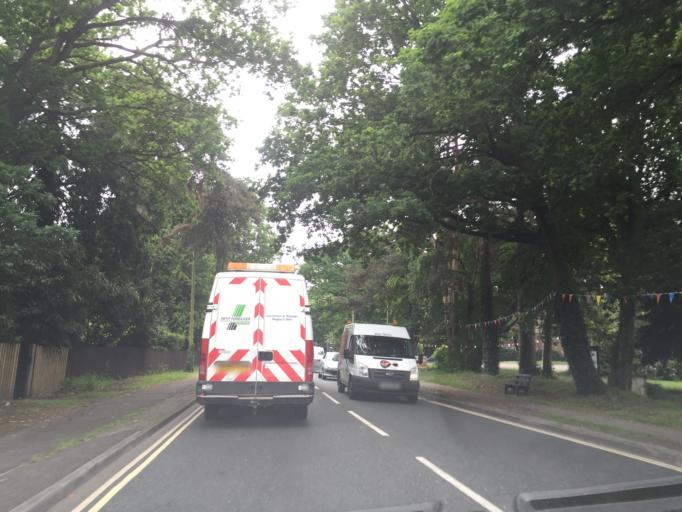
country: GB
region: England
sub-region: Dorset
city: Ferndown
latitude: 50.7995
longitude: -1.8927
